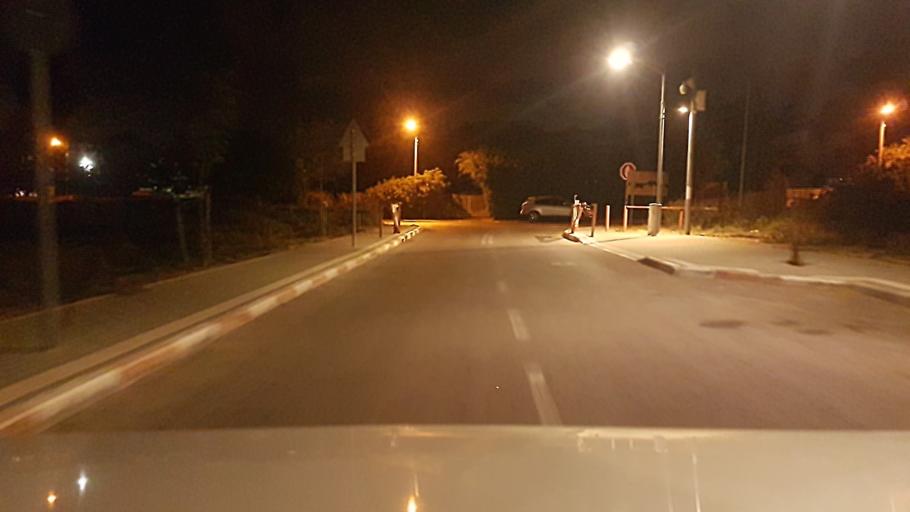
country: IL
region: Central District
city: Nehalim
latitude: 32.0769
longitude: 34.9155
